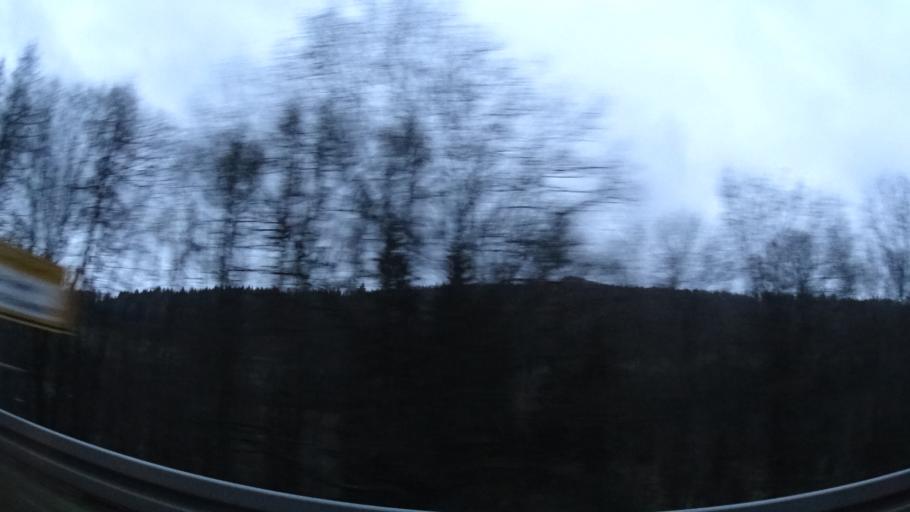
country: DE
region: Hesse
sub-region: Regierungsbezirk Kassel
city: Gersfeld
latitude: 50.4557
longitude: 9.8922
